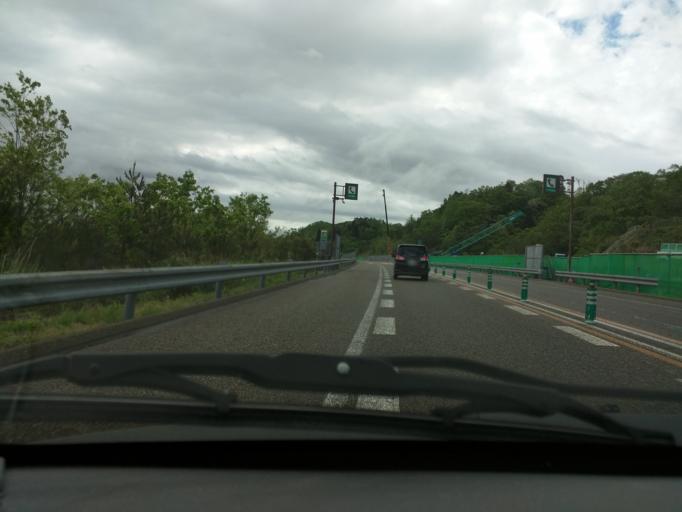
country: JP
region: Niigata
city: Joetsu
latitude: 37.1233
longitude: 138.2131
